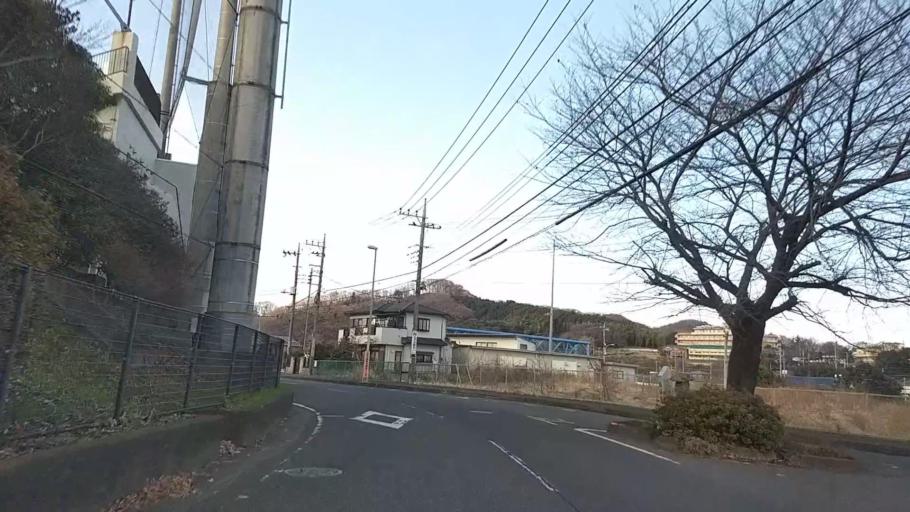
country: JP
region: Kanagawa
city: Atsugi
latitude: 35.4310
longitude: 139.3241
